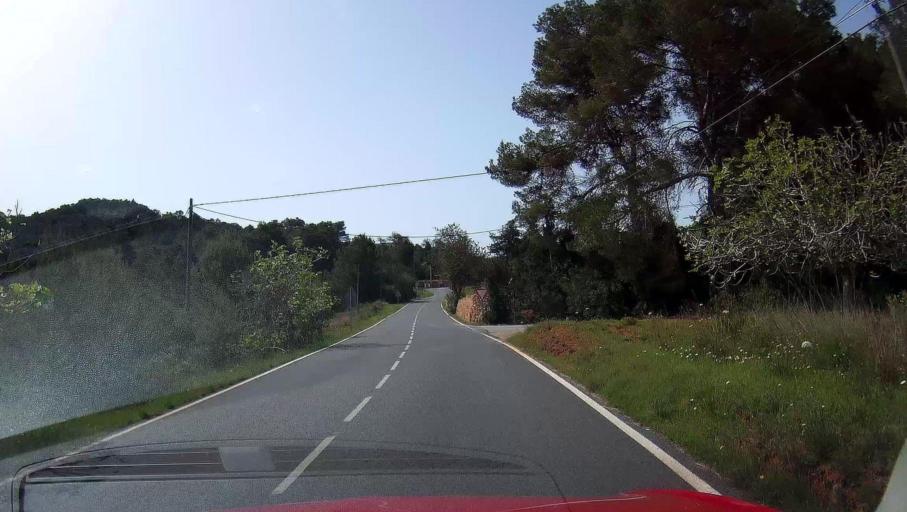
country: ES
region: Balearic Islands
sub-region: Illes Balears
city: Sant Joan de Labritja
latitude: 39.0409
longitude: 1.5660
